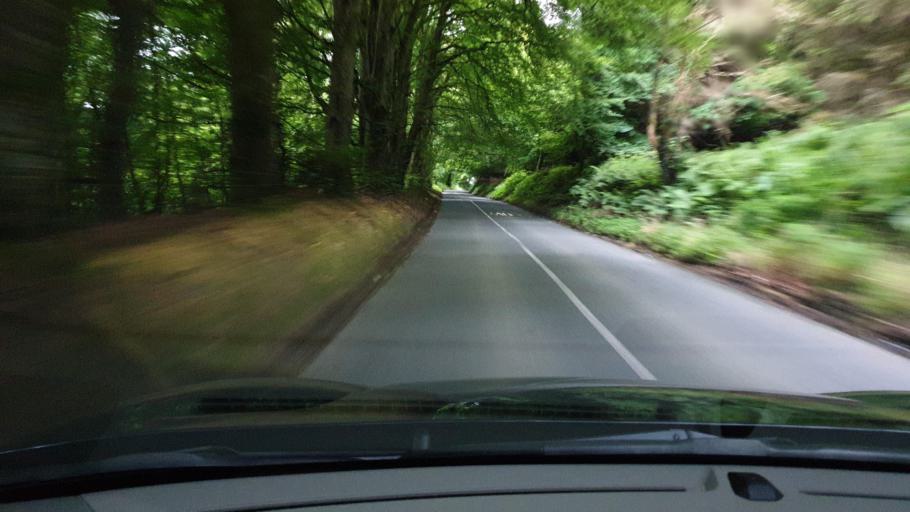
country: IE
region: Leinster
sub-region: South Dublin
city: Saggart
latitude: 53.2592
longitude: -6.4503
